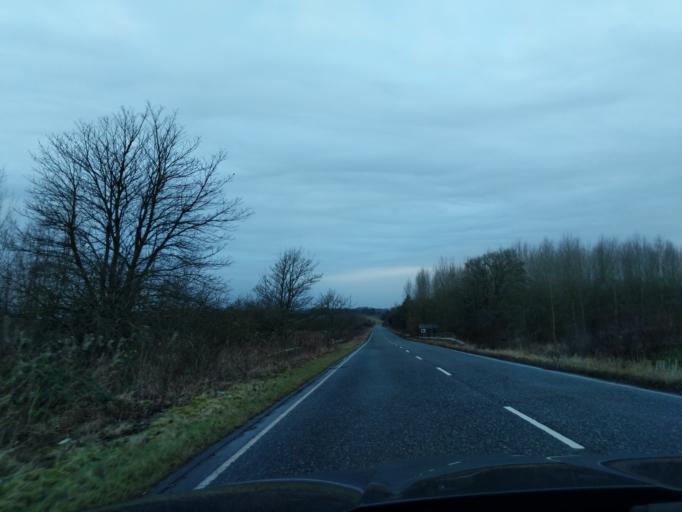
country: GB
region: England
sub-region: Northumberland
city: Rothley
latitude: 55.1389
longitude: -1.9748
